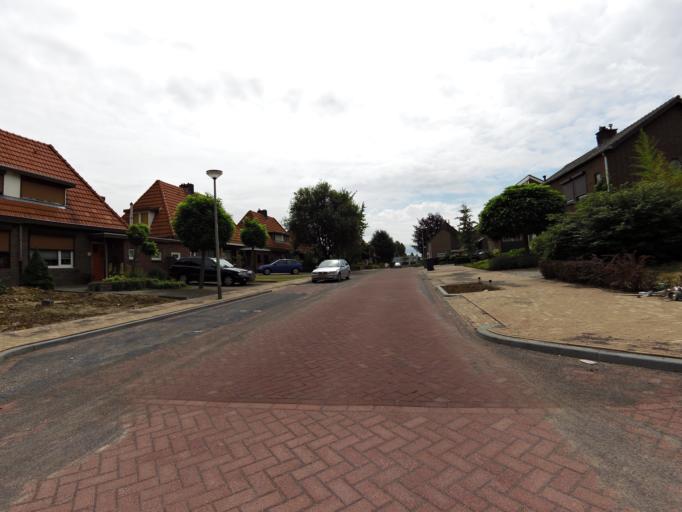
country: NL
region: Limburg
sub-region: Gemeente Kerkrade
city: Kerkrade
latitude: 50.9110
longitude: 6.0418
